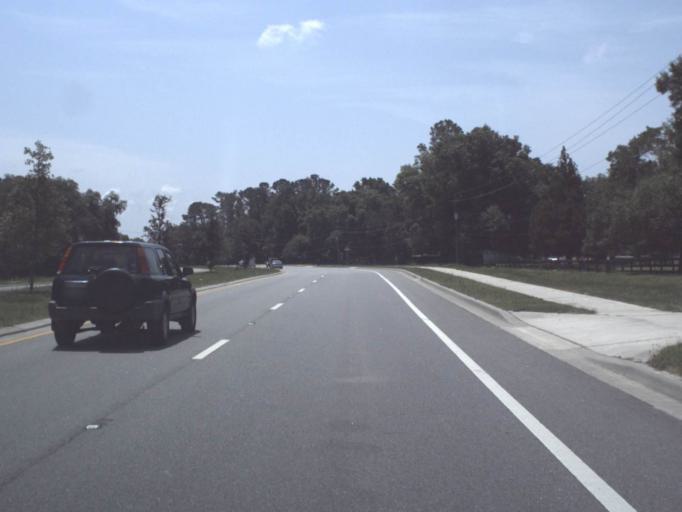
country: US
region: Florida
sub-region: Clay County
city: Green Cove Springs
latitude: 29.9664
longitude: -81.4980
